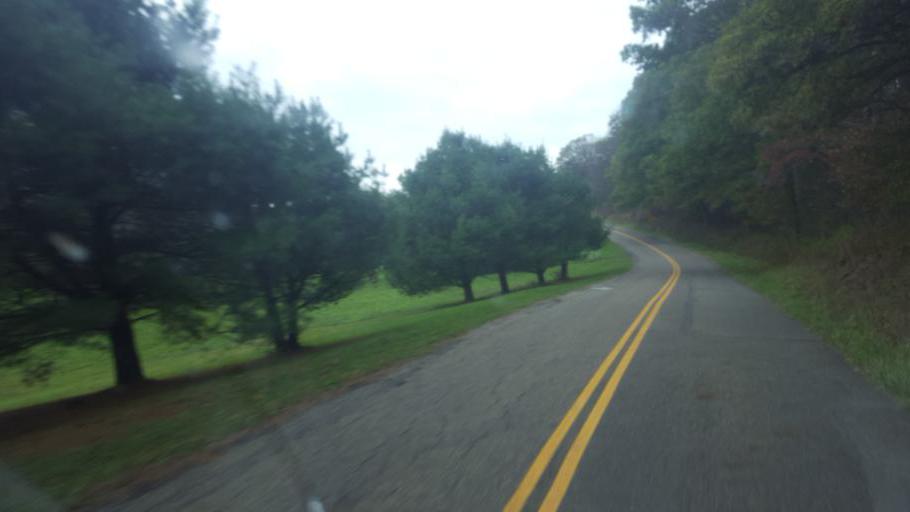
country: US
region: Ohio
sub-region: Carroll County
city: Carrollton
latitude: 40.4815
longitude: -81.0818
